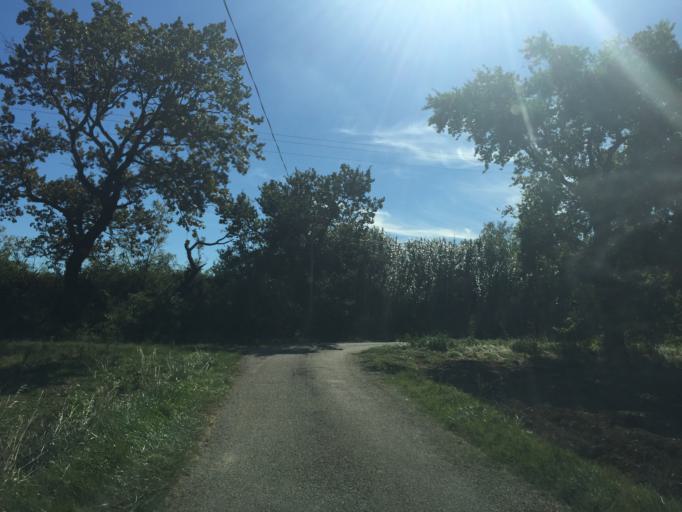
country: FR
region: Provence-Alpes-Cote d'Azur
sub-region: Departement du Vaucluse
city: Piolenc
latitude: 44.1509
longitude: 4.7702
